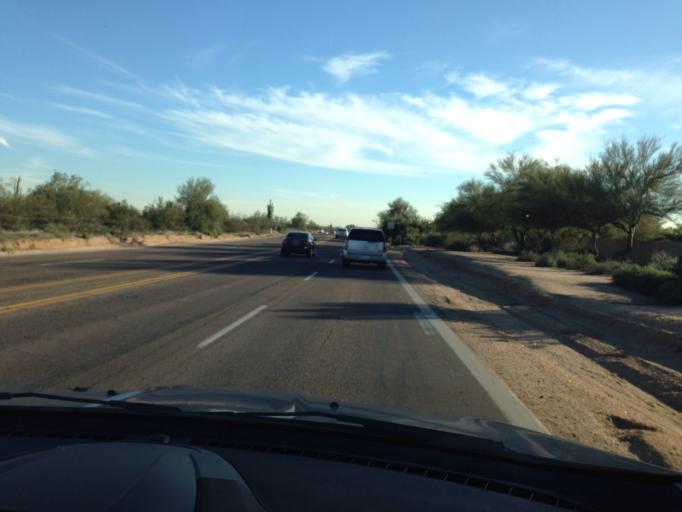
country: US
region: Arizona
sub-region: Maricopa County
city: Cave Creek
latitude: 33.7329
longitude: -111.9782
